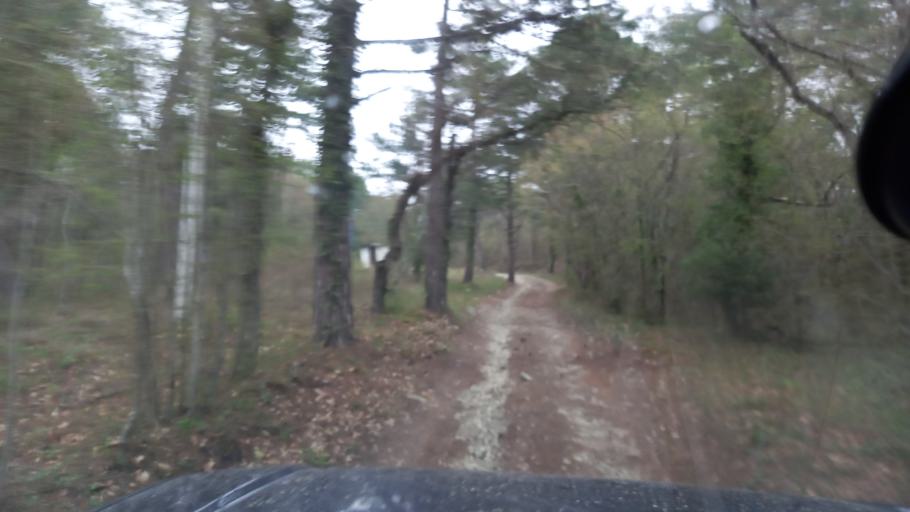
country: RU
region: Krasnodarskiy
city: Dzhubga
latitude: 44.3178
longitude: 38.6648
